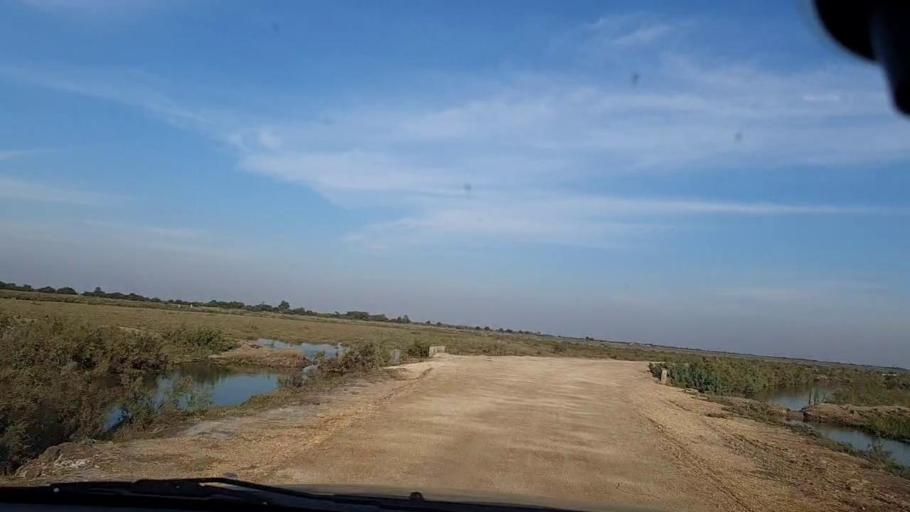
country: PK
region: Sindh
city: Mirpur Batoro
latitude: 24.6579
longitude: 68.3055
